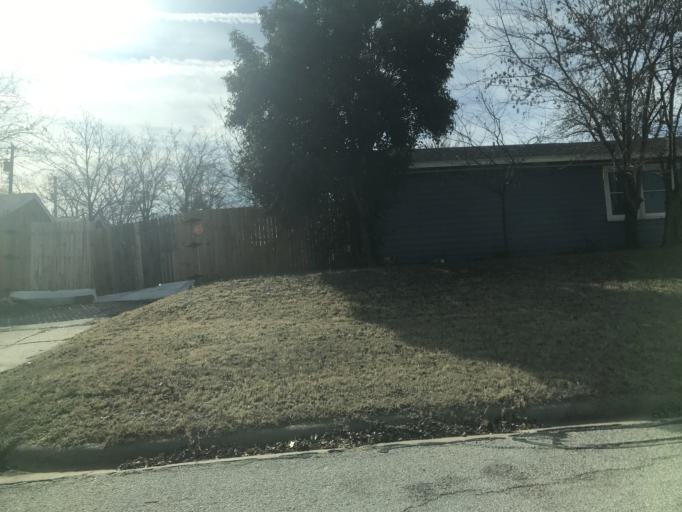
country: US
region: Texas
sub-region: Taylor County
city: Abilene
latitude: 32.4448
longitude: -99.7395
